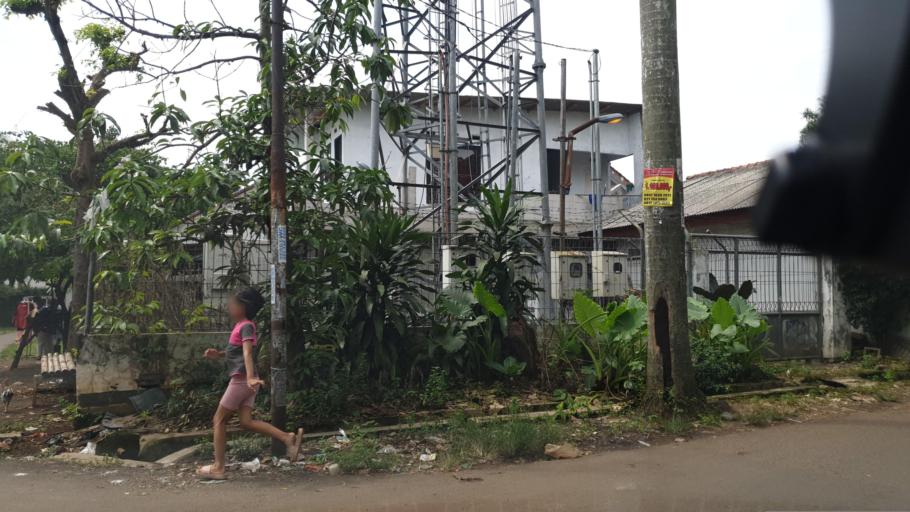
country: ID
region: West Java
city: Pamulang
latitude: -6.3511
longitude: 106.7674
